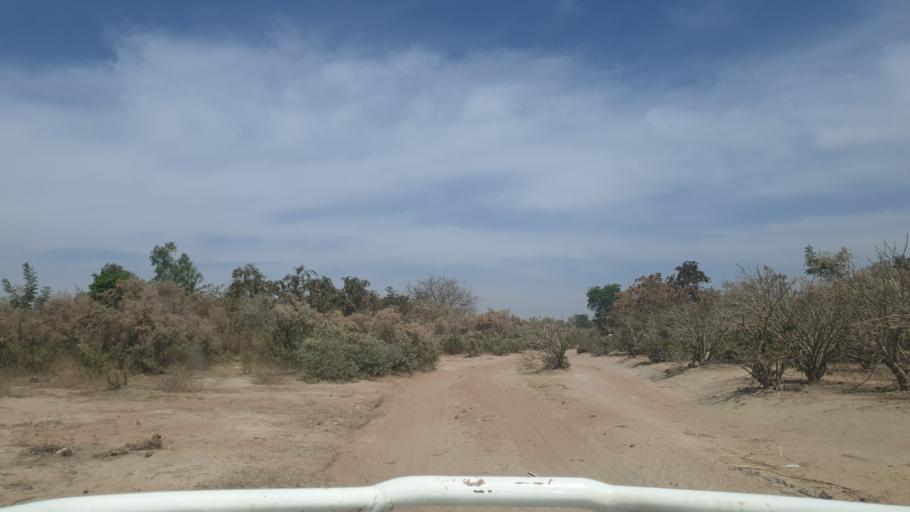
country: ML
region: Sikasso
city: Yorosso
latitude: 12.2802
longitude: -4.6876
